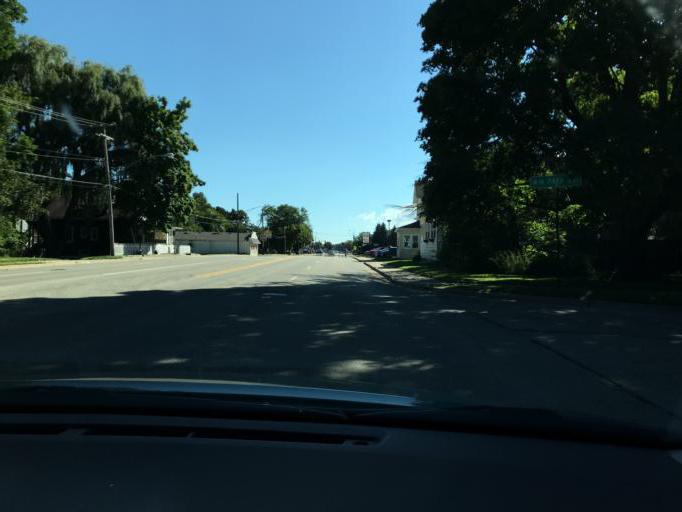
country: US
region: Illinois
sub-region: Lake County
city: Winthrop Harbor
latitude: 42.4854
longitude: -87.8223
